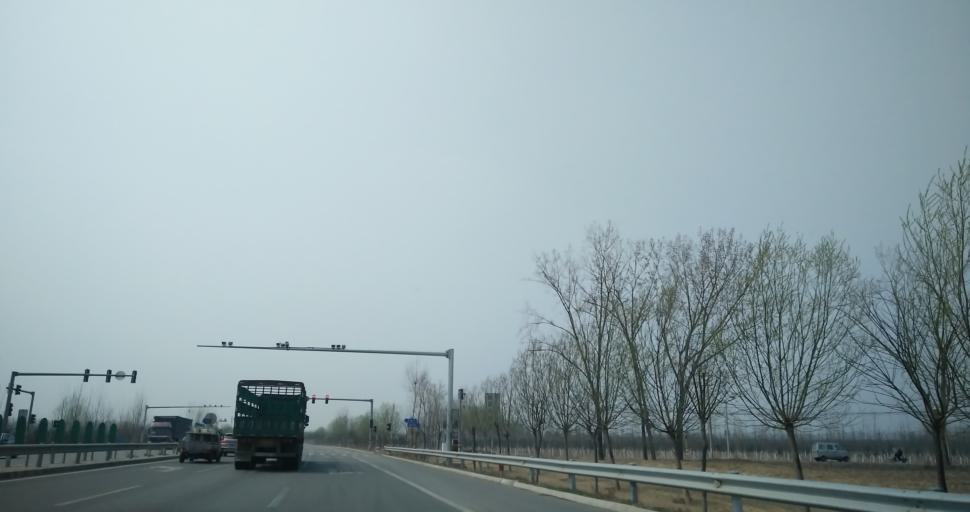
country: CN
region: Beijing
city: Weishanzhuang
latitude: 39.6787
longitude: 116.4340
